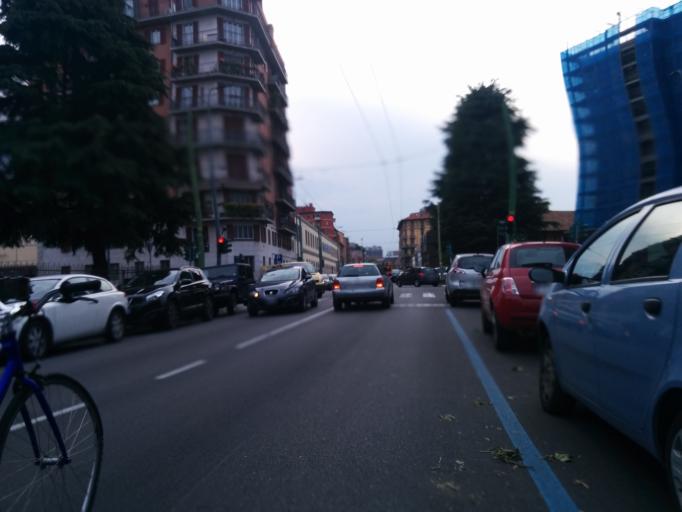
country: IT
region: Lombardy
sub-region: Citta metropolitana di Milano
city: Milano
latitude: 45.4500
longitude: 9.2153
